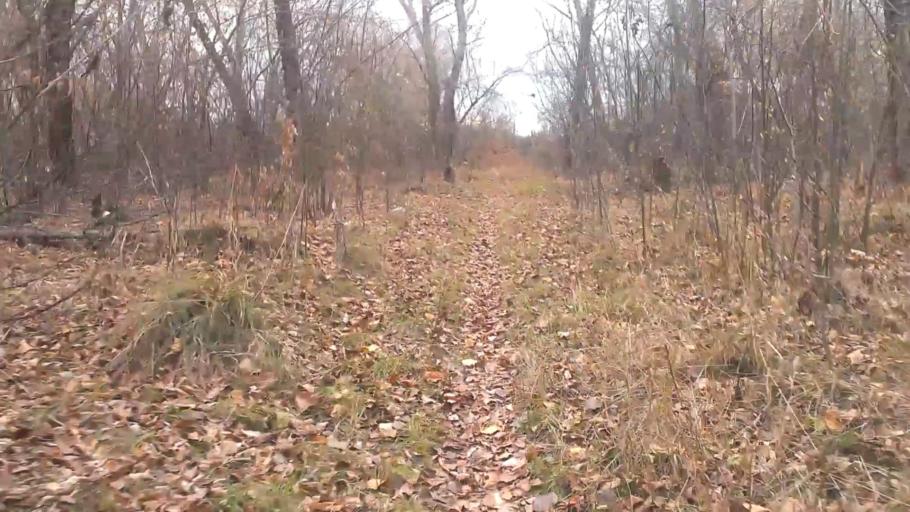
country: RU
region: Altai Krai
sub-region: Gorod Barnaulskiy
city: Barnaul
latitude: 53.3658
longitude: 83.7281
